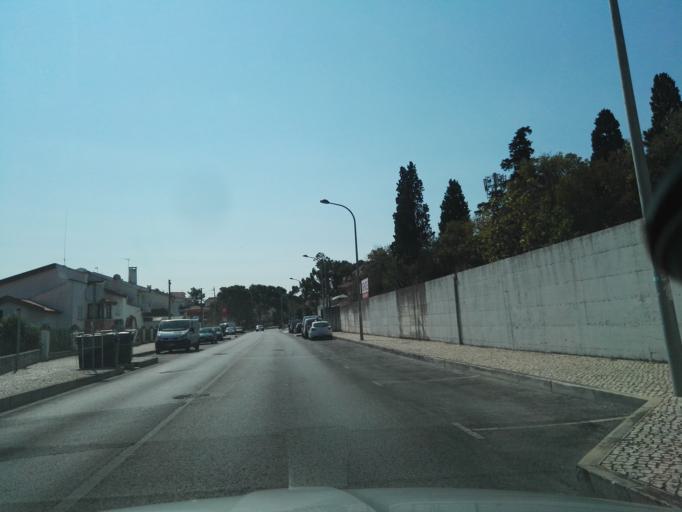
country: PT
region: Lisbon
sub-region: Cascais
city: Estoril
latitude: 38.7126
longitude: -9.3868
